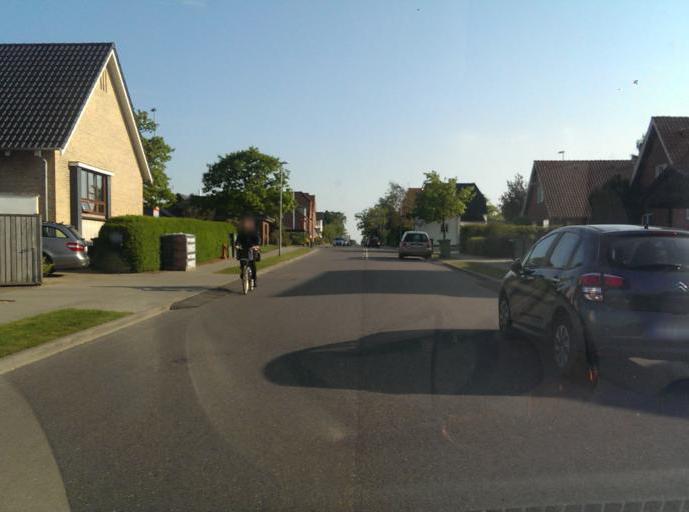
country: DK
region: South Denmark
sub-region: Esbjerg Kommune
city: Esbjerg
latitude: 55.4791
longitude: 8.4534
